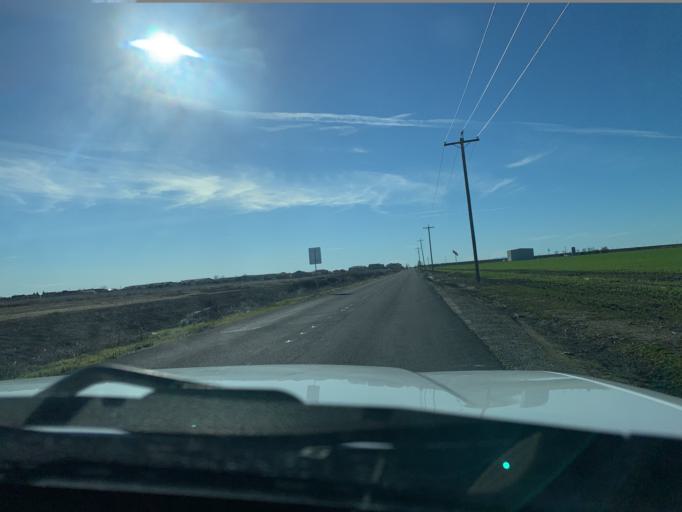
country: US
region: California
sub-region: Yolo County
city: Woodland
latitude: 38.6527
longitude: -121.7473
